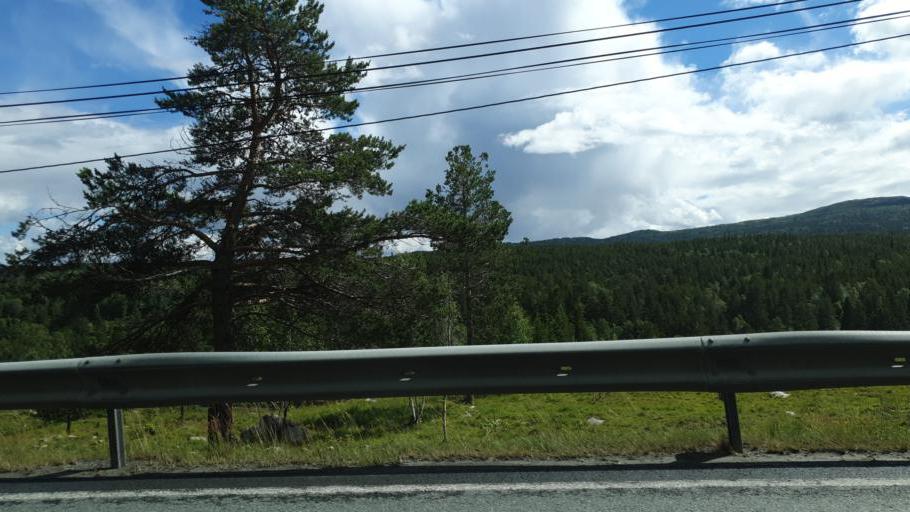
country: NO
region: Sor-Trondelag
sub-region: Rennebu
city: Berkak
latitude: 62.7010
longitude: 9.9481
